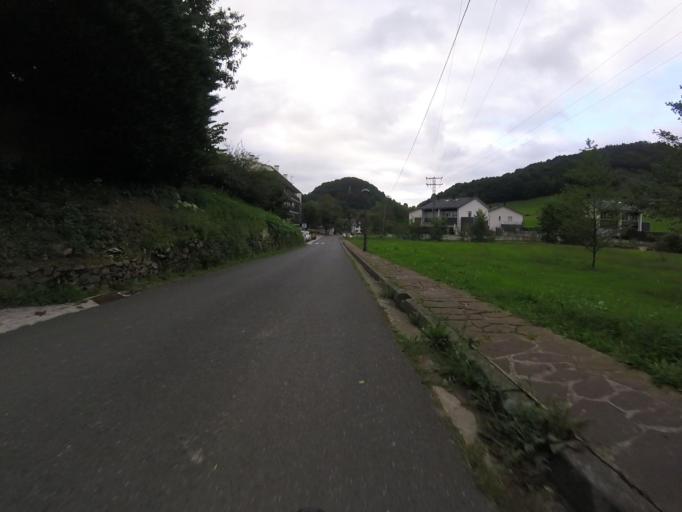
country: ES
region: Basque Country
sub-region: Provincia de Guipuzcoa
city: Errenteria
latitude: 43.2819
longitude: -1.8517
